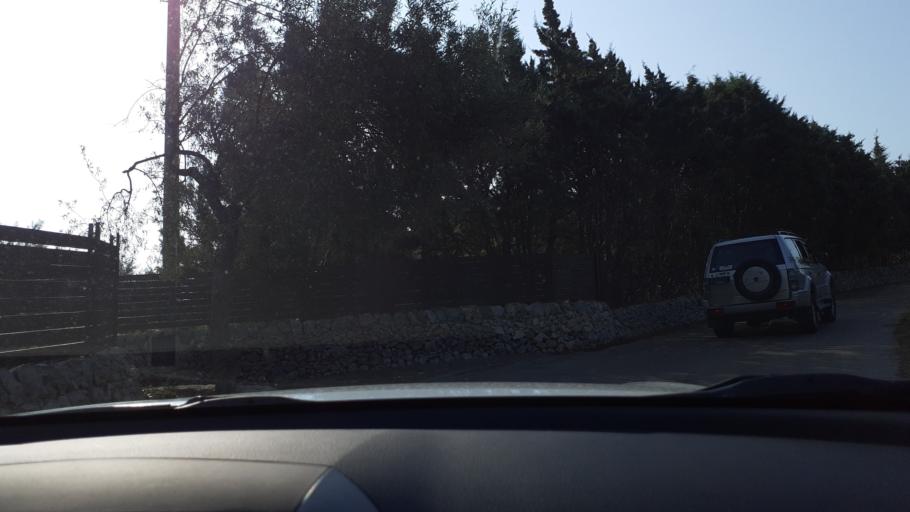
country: IT
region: Sicily
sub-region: Provincia di Siracusa
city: Cassibile
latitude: 36.9764
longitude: 15.1584
